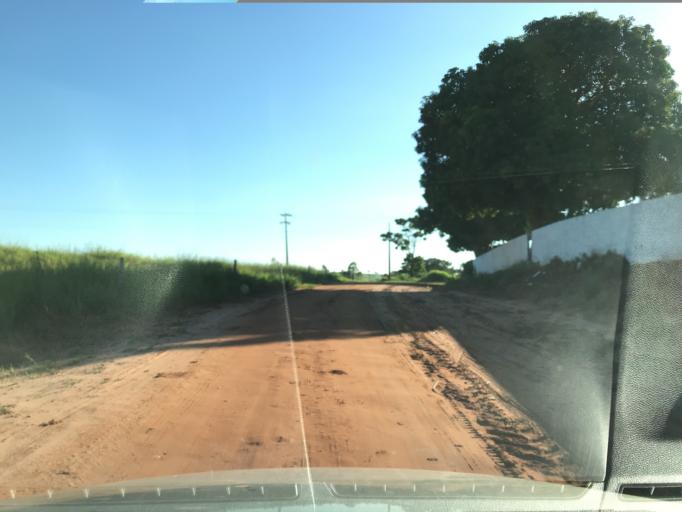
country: BR
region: Parana
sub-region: Ipora
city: Ipora
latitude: -23.9977
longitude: -53.7216
